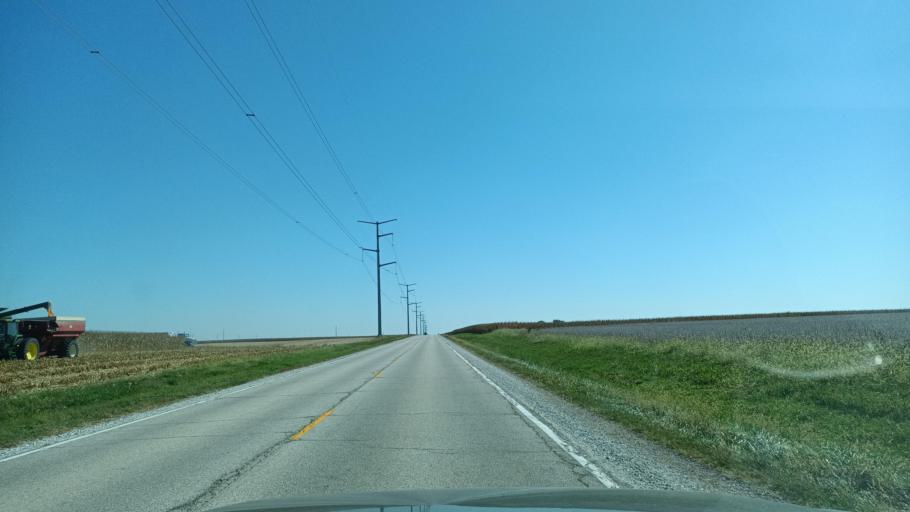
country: US
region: Illinois
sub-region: Peoria County
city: Elmwood
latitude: 40.9022
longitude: -89.9967
